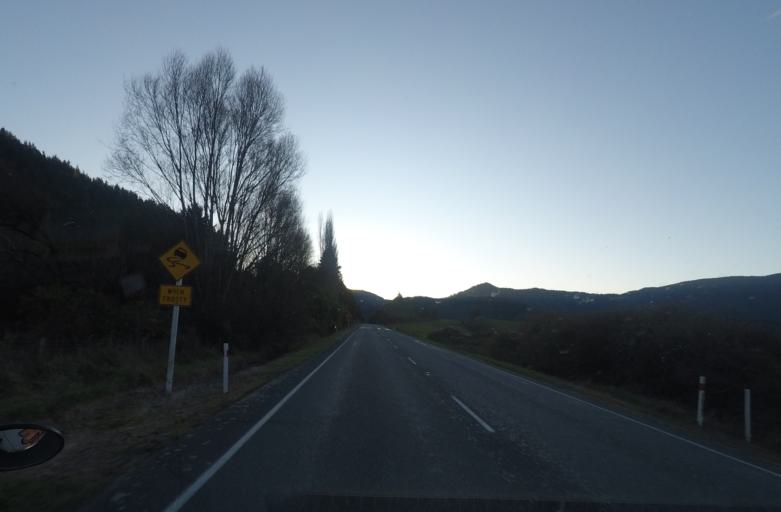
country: NZ
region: Marlborough
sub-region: Marlborough District
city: Picton
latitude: -41.2857
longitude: 173.6617
